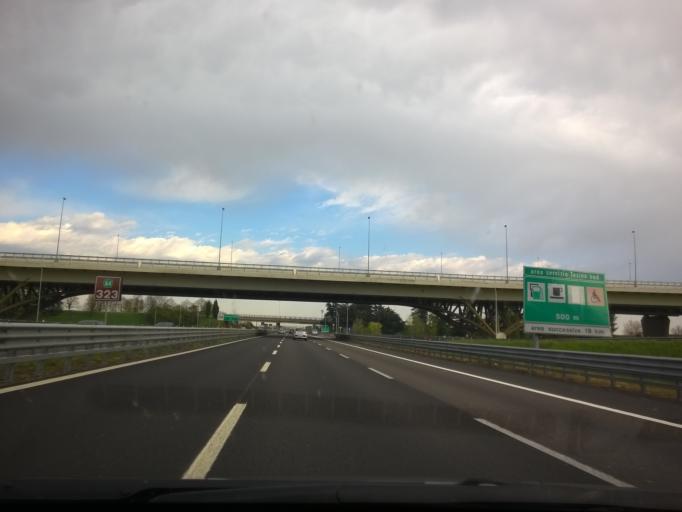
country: IT
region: Veneto
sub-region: Provincia di Vicenza
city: Torri di Quartesolo
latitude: 45.5069
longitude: 11.6173
